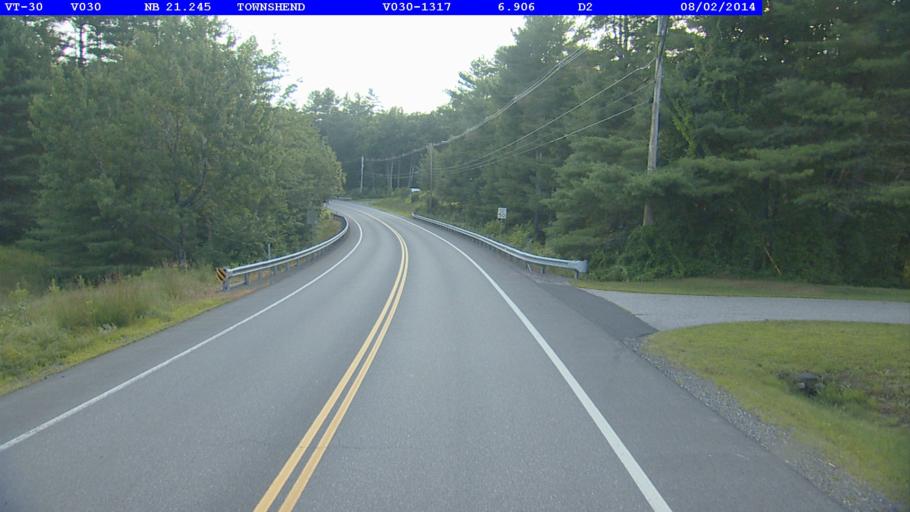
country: US
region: Vermont
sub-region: Windham County
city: Newfane
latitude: 43.0851
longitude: -72.7186
